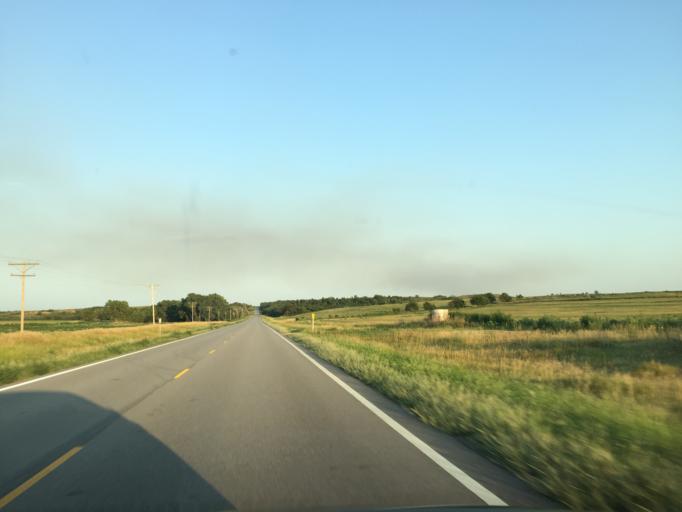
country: US
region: Kansas
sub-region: Ellsworth County
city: Ellsworth
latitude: 38.7073
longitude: -98.2281
